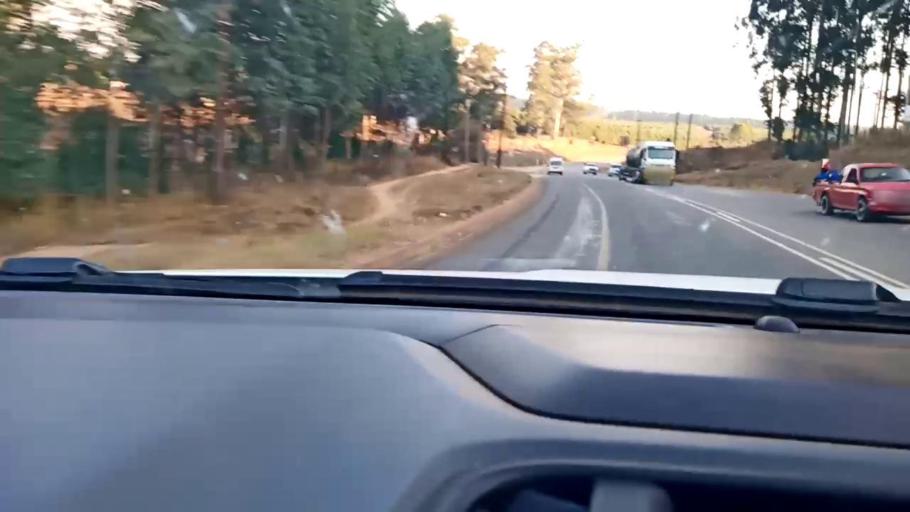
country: ZA
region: Limpopo
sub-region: Mopani District Municipality
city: Duiwelskloof
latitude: -23.7084
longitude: 30.1303
